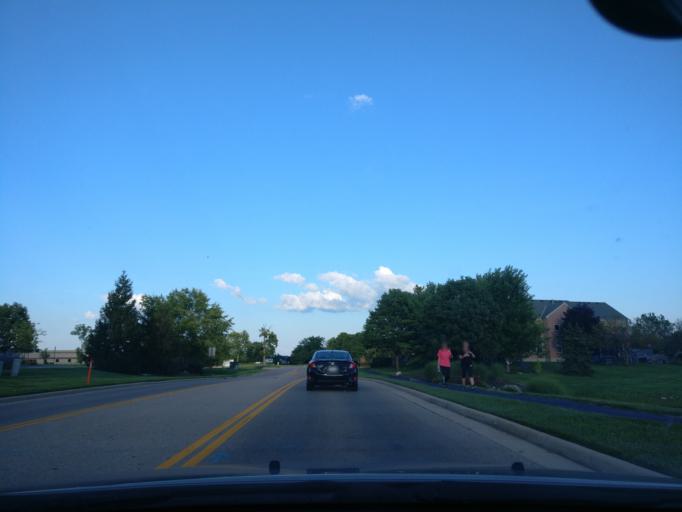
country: US
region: Ohio
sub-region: Warren County
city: Springboro
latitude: 39.5793
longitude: -84.2257
